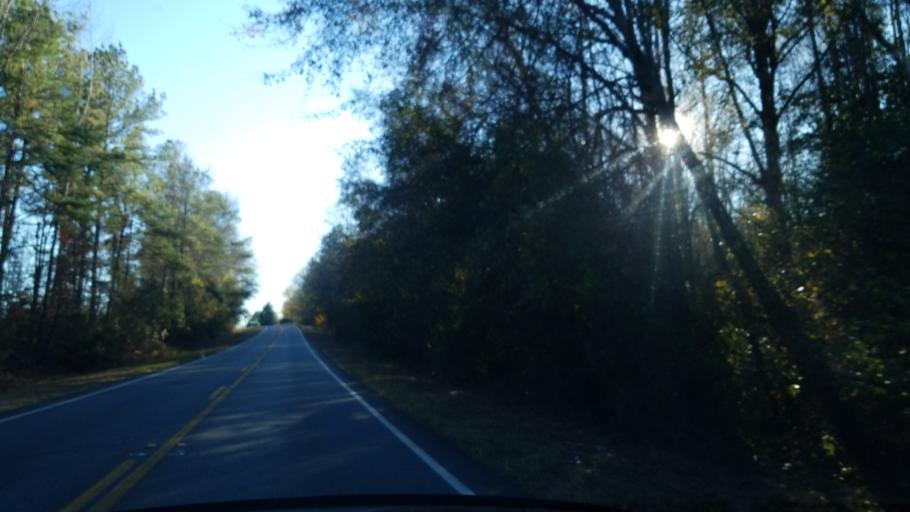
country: US
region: Georgia
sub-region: Talbot County
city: Talbotton
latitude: 32.5407
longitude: -84.6024
